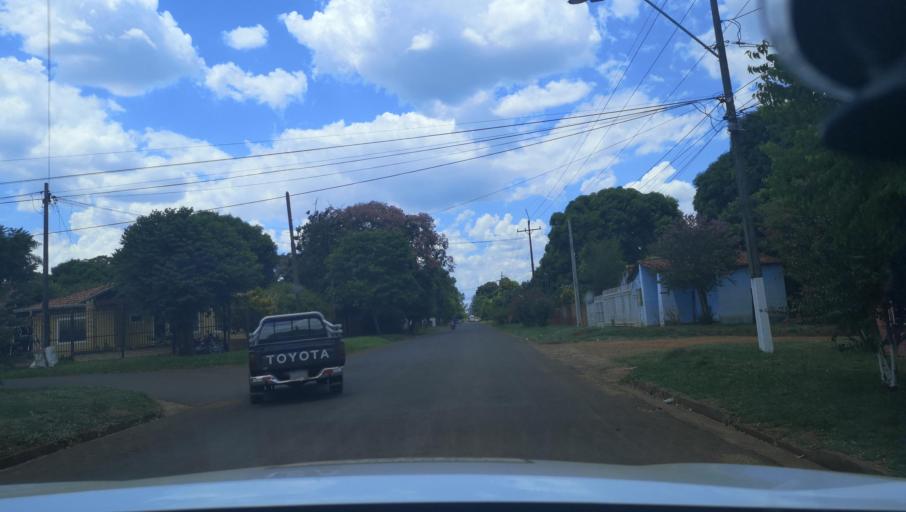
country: PY
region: Itapua
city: Carmen del Parana
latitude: -27.1706
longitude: -56.2359
